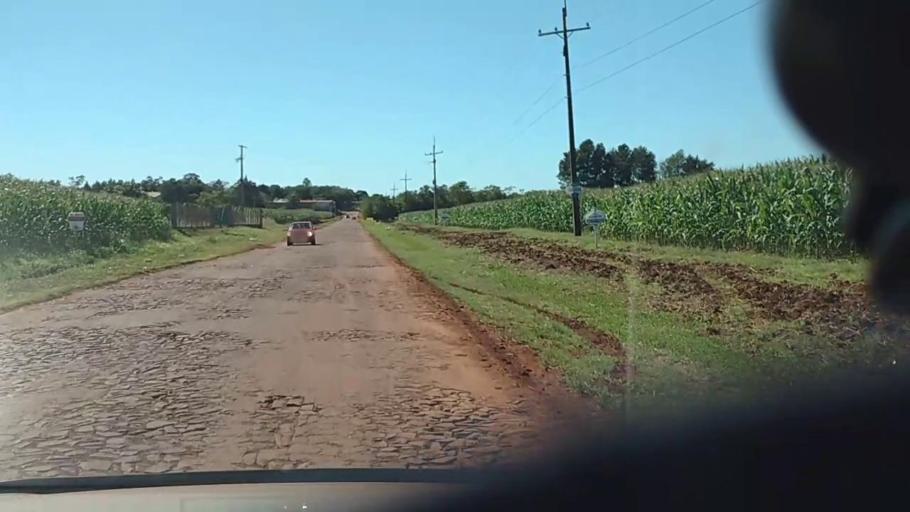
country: PY
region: Alto Parana
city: Naranjal
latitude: -25.9532
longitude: -55.1306
